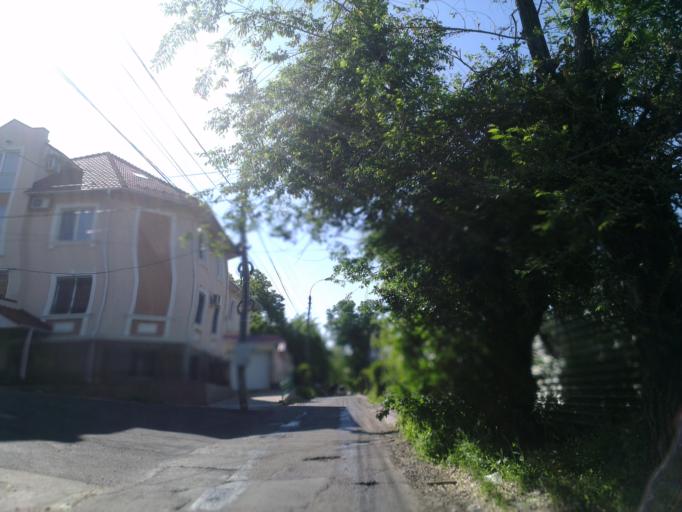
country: MD
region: Chisinau
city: Chisinau
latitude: 47.0158
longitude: 28.8234
